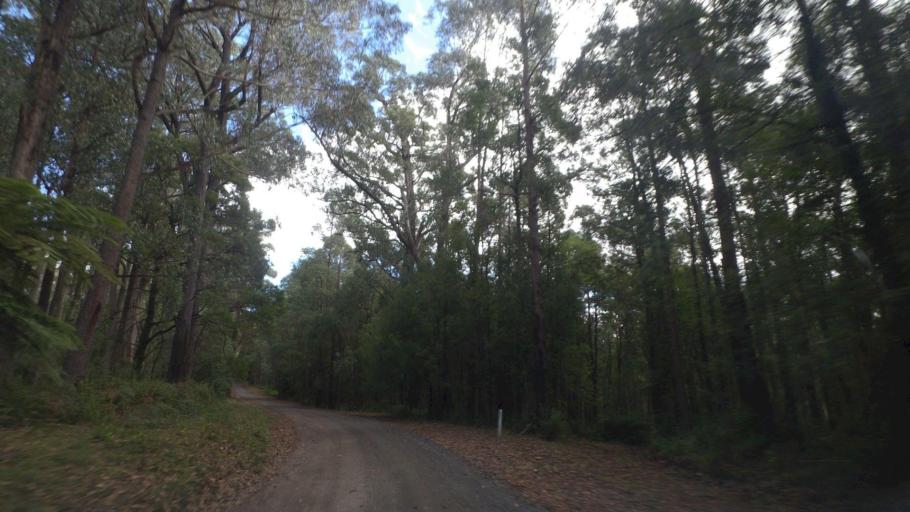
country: AU
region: Victoria
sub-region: Cardinia
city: Gembrook
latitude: -37.8958
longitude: 145.6662
